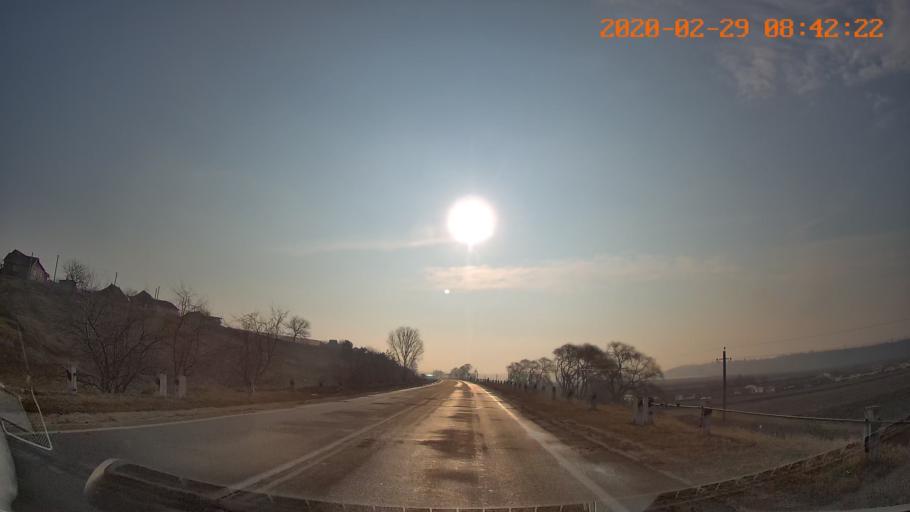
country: MD
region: Anenii Noi
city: Varnita
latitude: 46.9228
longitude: 29.4495
